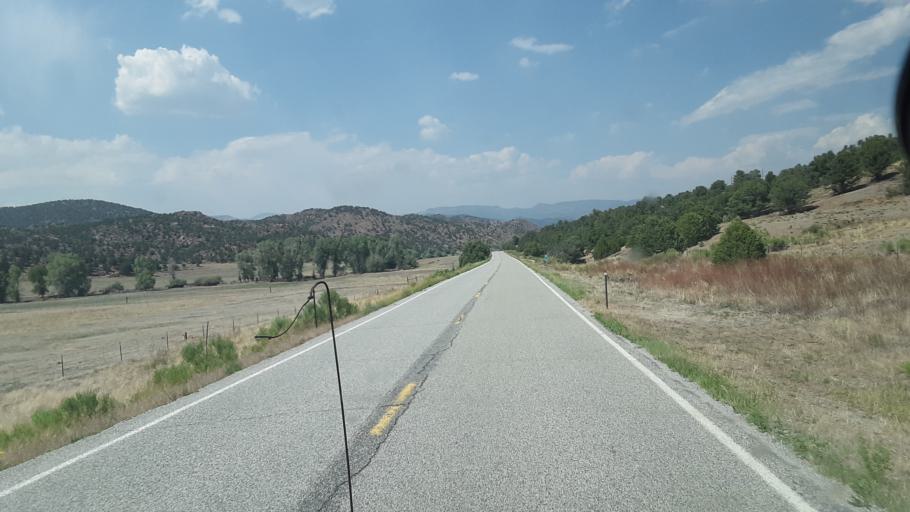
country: US
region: Colorado
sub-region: Custer County
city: Westcliffe
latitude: 38.3441
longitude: -105.5952
